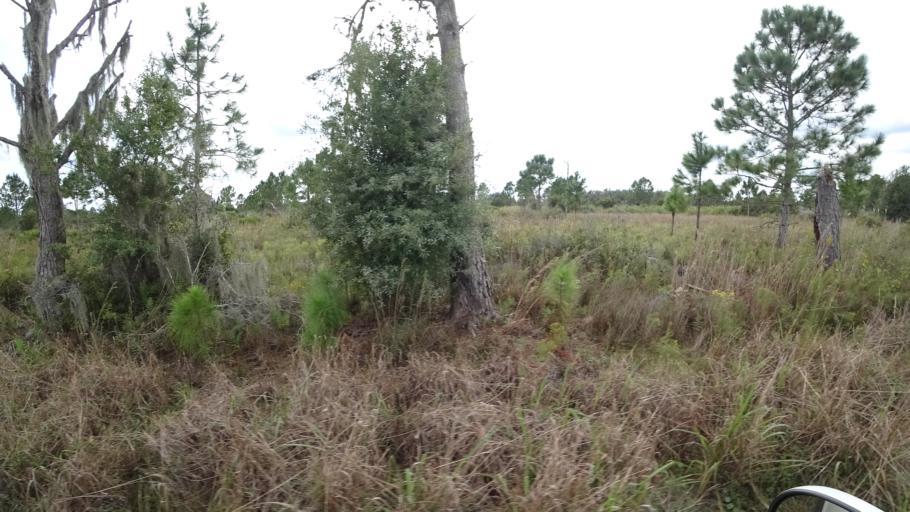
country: US
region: Florida
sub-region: Hillsborough County
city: Wimauma
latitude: 27.5535
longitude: -82.1337
